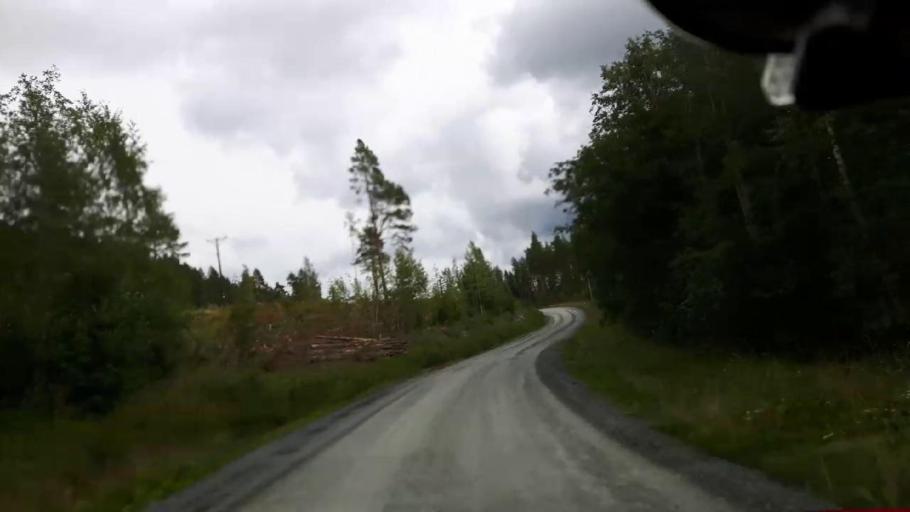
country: SE
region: Jaemtland
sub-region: Krokoms Kommun
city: Krokom
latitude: 63.5813
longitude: 14.1897
